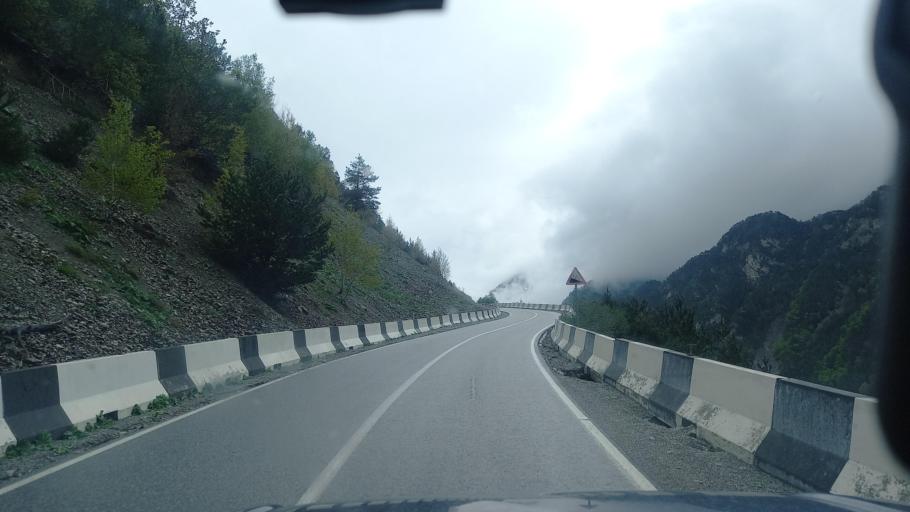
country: RU
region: North Ossetia
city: Mizur
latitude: 42.7924
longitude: 43.9992
